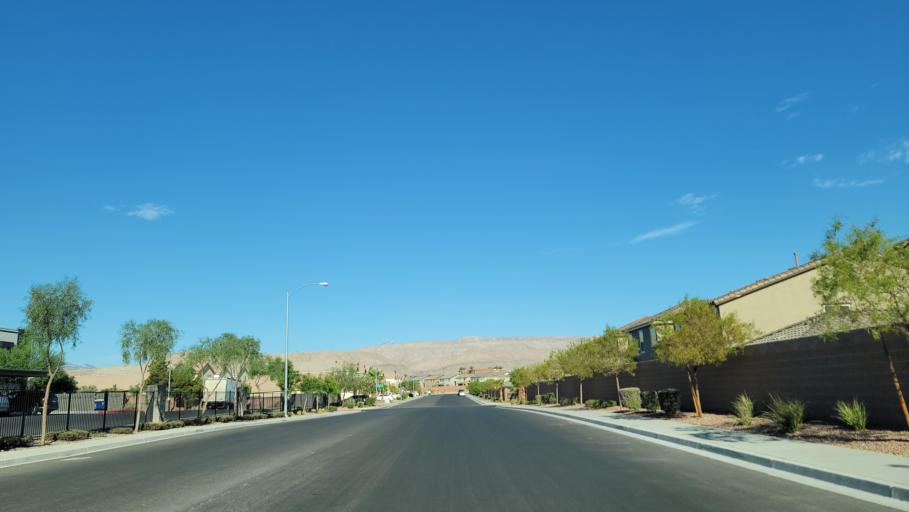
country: US
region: Nevada
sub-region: Clark County
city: Spring Valley
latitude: 36.0815
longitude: -115.2829
